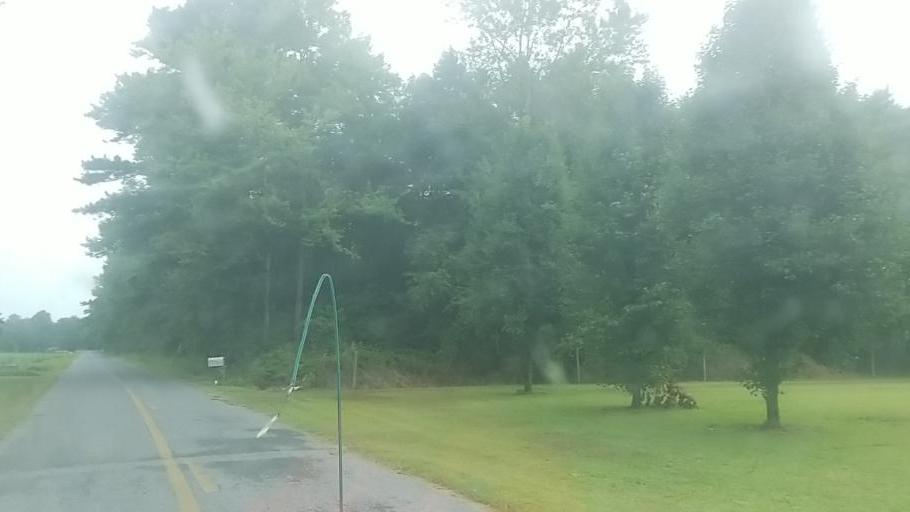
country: US
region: Delaware
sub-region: Sussex County
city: Selbyville
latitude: 38.4245
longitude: -75.2880
